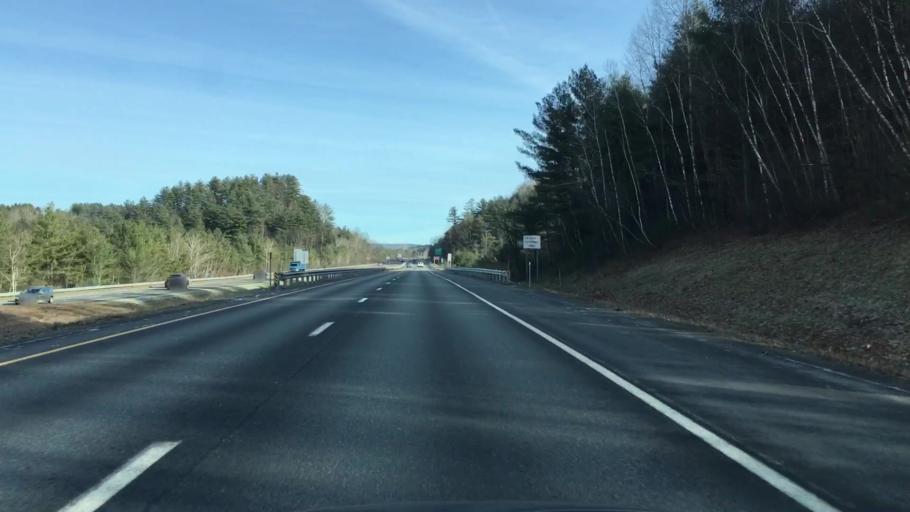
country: US
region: Vermont
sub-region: Windsor County
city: White River Junction
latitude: 43.6314
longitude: -72.3092
